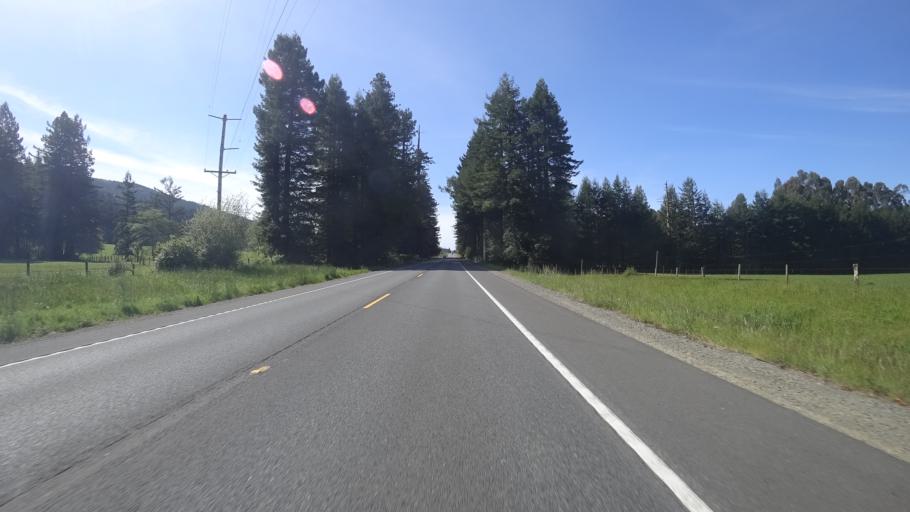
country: US
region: California
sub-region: Del Norte County
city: Bertsch-Oceanview
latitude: 41.9055
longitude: -124.1366
